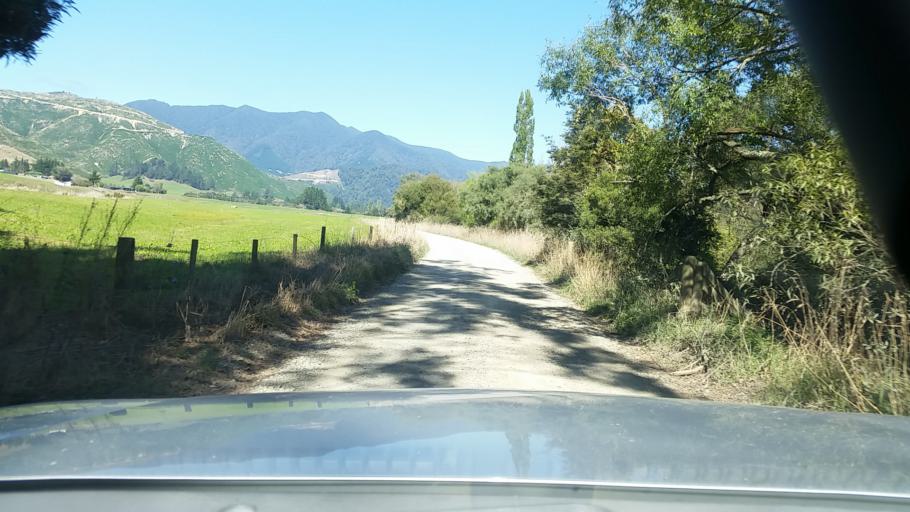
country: NZ
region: Nelson
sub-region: Nelson City
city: Nelson
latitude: -41.2639
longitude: 173.5763
